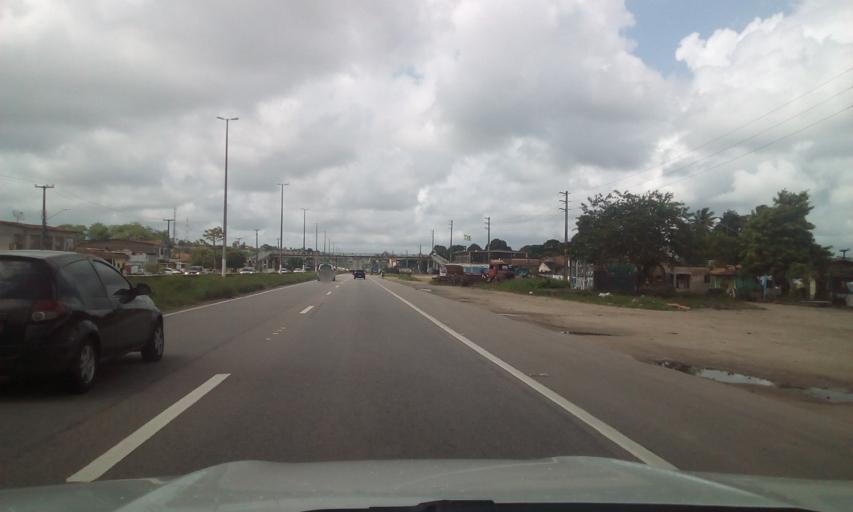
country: BR
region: Pernambuco
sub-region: Igarassu
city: Igarassu
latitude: -7.8251
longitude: -34.9157
